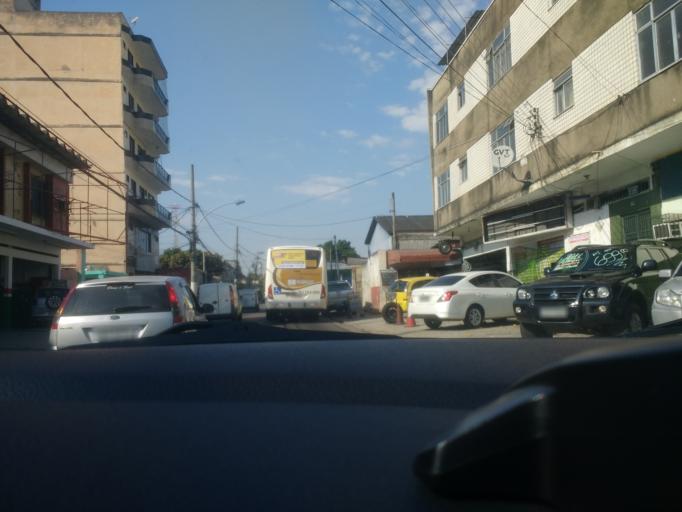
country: BR
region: Rio de Janeiro
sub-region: Duque De Caxias
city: Duque de Caxias
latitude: -22.7987
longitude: -43.2945
